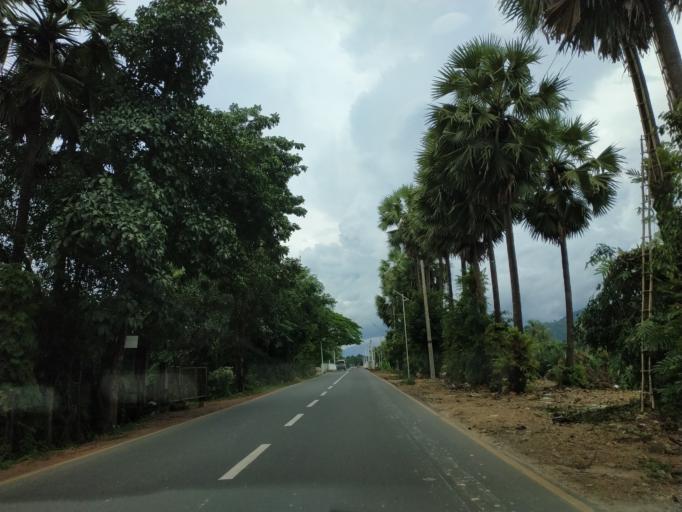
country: MM
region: Tanintharyi
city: Dawei
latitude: 14.0705
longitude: 98.2168
